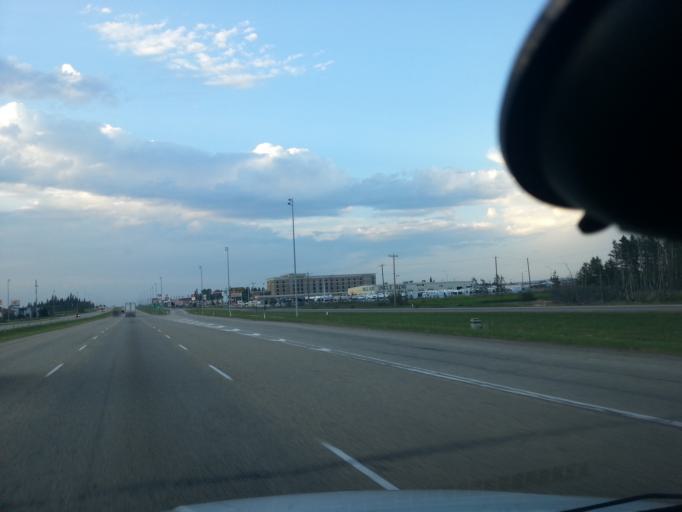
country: CA
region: Alberta
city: Red Deer
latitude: 52.2103
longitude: -113.8137
